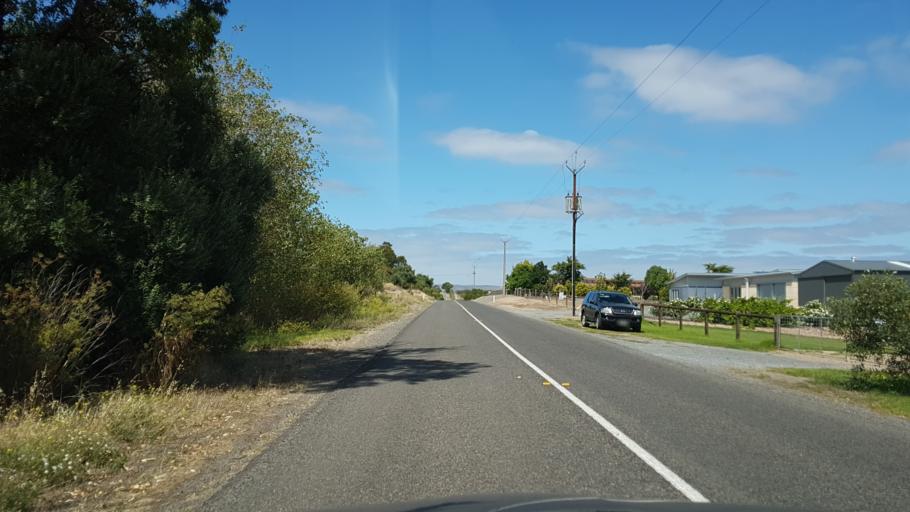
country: AU
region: South Australia
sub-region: Onkaparinga
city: McLaren Vale
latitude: -35.2166
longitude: 138.5178
